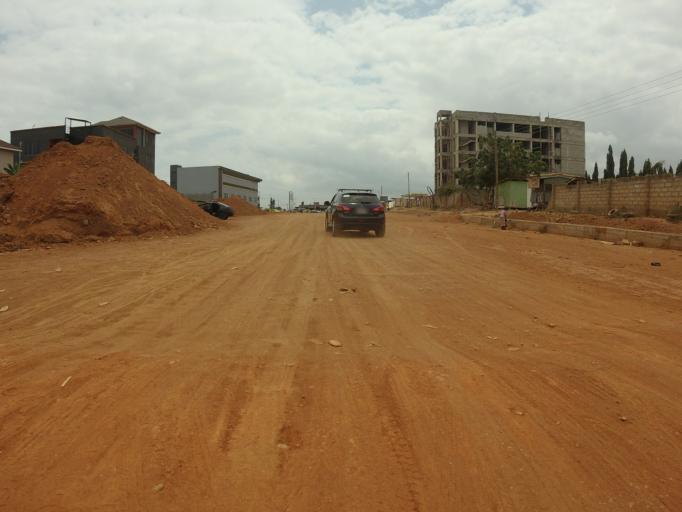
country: GH
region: Greater Accra
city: Medina Estates
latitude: 5.6256
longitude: -0.1511
